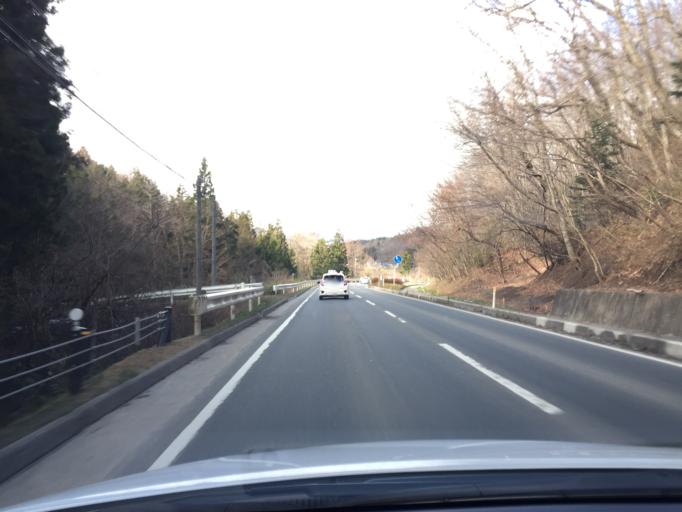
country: JP
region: Miyagi
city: Marumori
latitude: 37.6883
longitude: 140.7761
